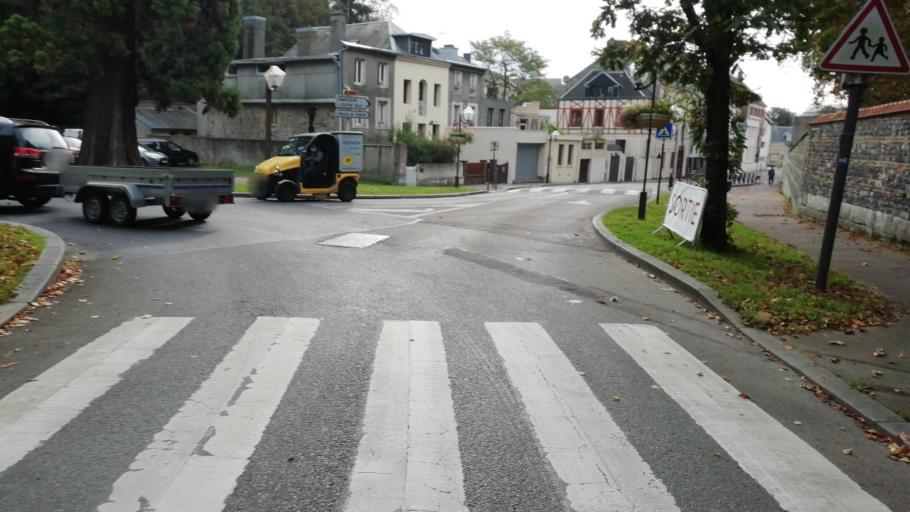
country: FR
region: Haute-Normandie
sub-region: Departement de la Seine-Maritime
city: Harfleur
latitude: 49.5094
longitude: 0.2011
